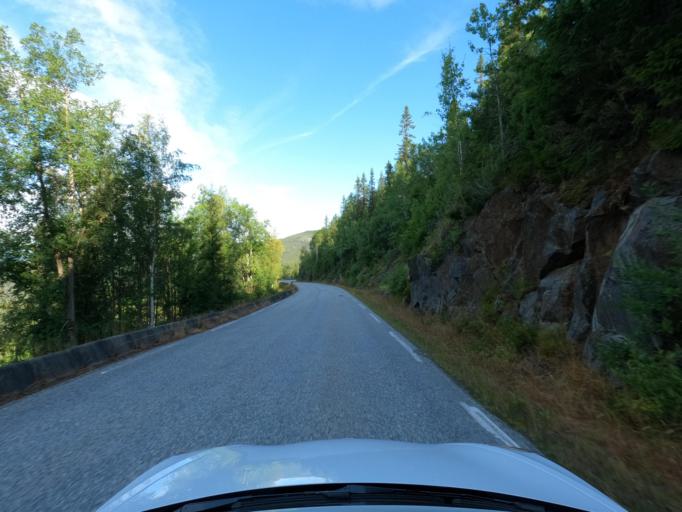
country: NO
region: Telemark
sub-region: Hjartdal
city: Sauland
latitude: 59.9167
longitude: 8.9823
